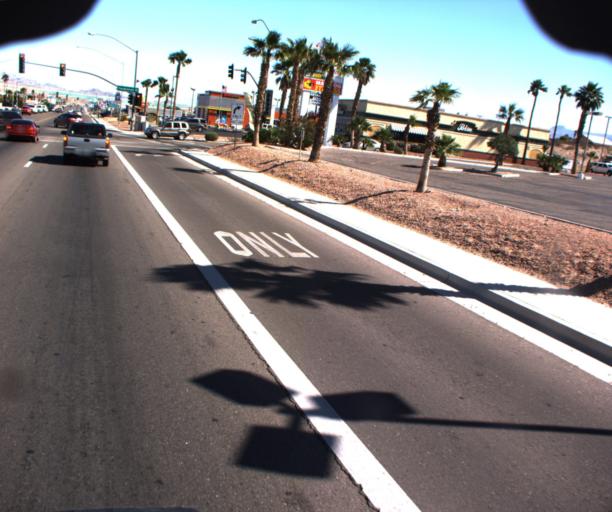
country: US
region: Arizona
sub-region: Mohave County
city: Bullhead City
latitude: 35.1051
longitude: -114.5979
